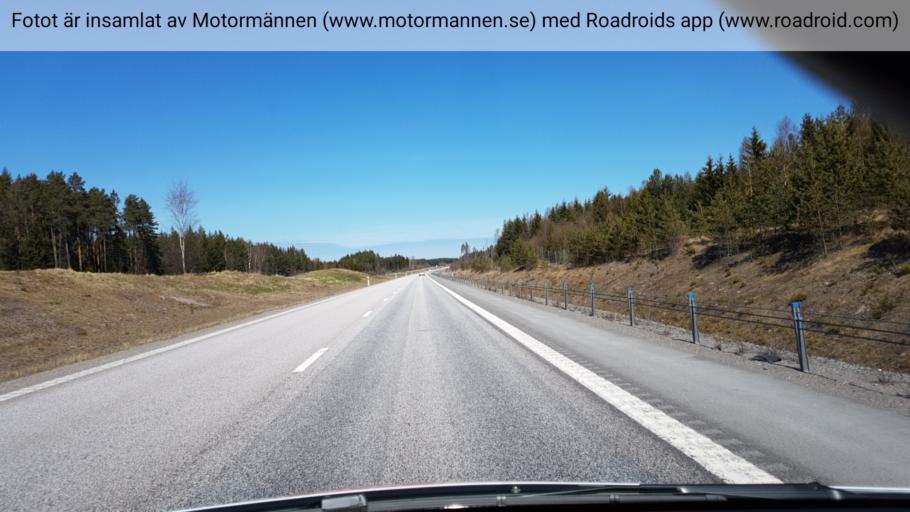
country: SE
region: Uppsala
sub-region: Tierps Kommun
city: Tierp
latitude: 60.2571
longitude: 17.5005
